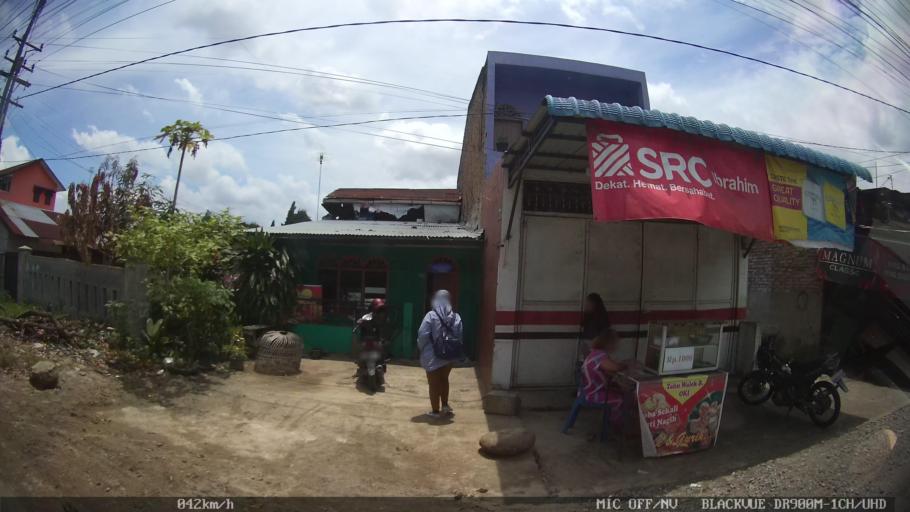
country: ID
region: North Sumatra
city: Medan
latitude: 3.6161
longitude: 98.6942
